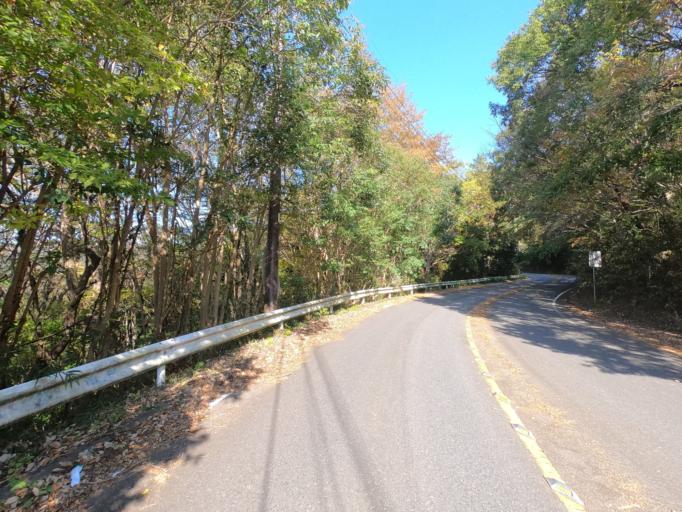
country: JP
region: Ibaraki
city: Tsukuba
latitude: 36.1652
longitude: 140.1746
